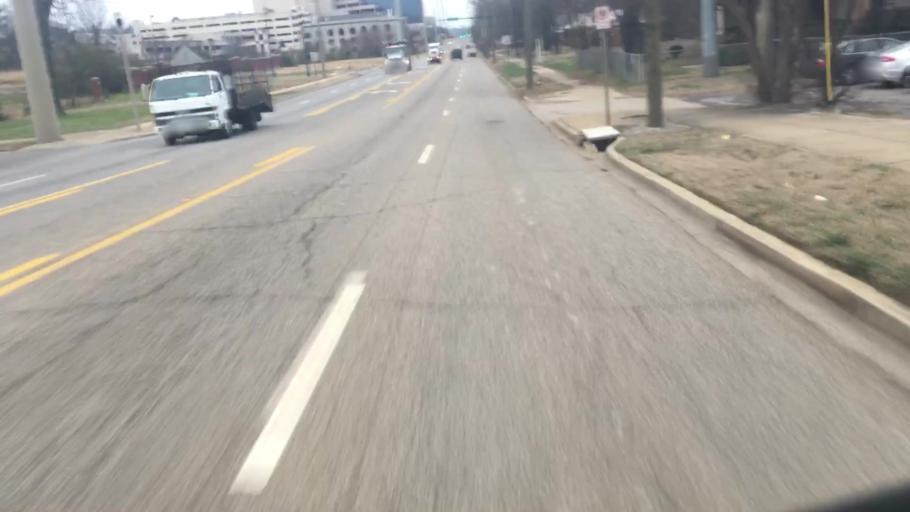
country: US
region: Alabama
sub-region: Jefferson County
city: Birmingham
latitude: 33.5323
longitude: -86.8067
